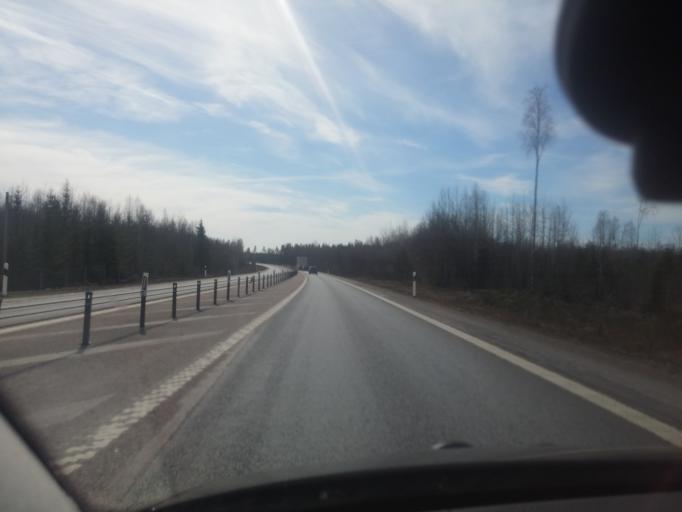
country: SE
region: Gaevleborg
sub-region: Gavle Kommun
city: Gavle
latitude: 60.7780
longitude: 17.0716
